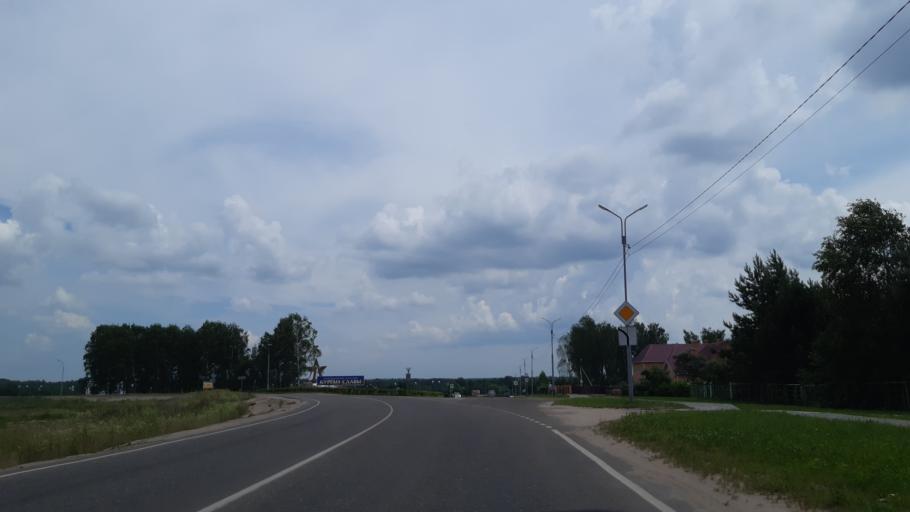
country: RU
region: Smolensk
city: Desnogorsk
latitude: 54.1554
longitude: 33.3028
